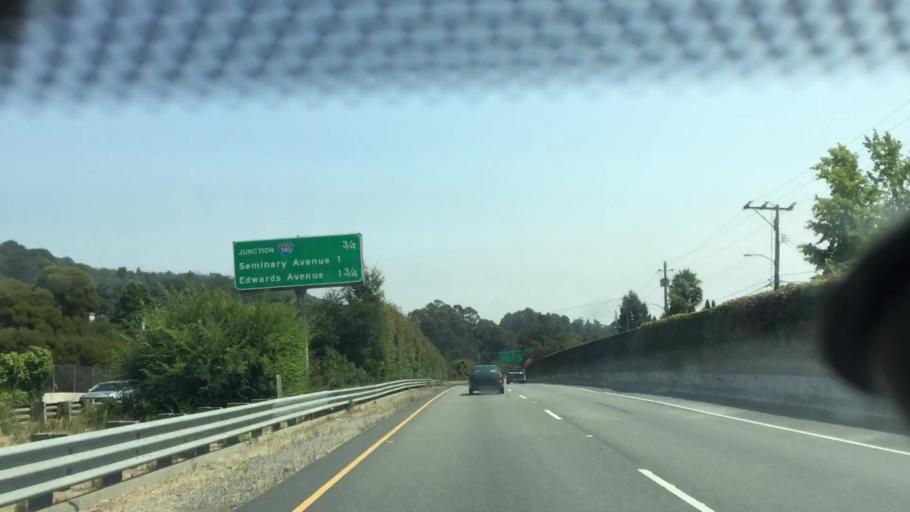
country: US
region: California
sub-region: Alameda County
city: Piedmont
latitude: 37.7965
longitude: -122.1838
